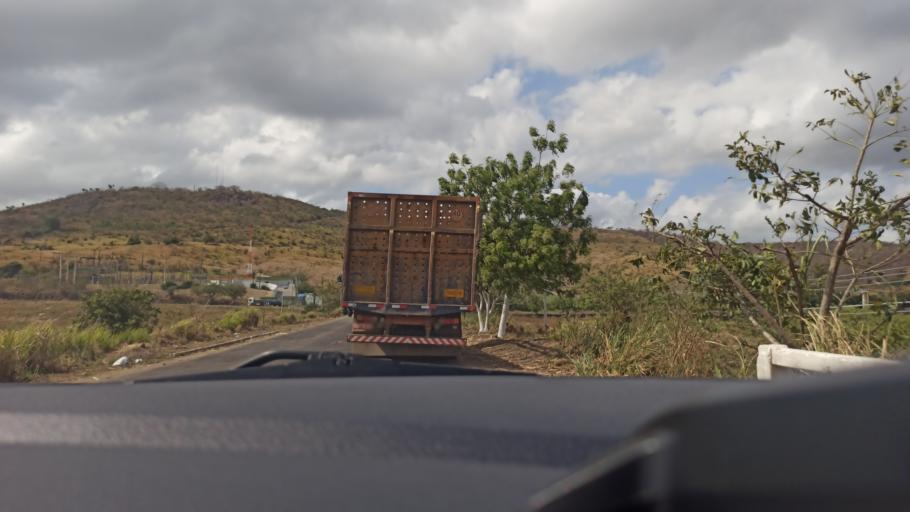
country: BR
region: Pernambuco
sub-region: Timbauba
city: Timbauba
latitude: -7.5187
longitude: -35.3049
